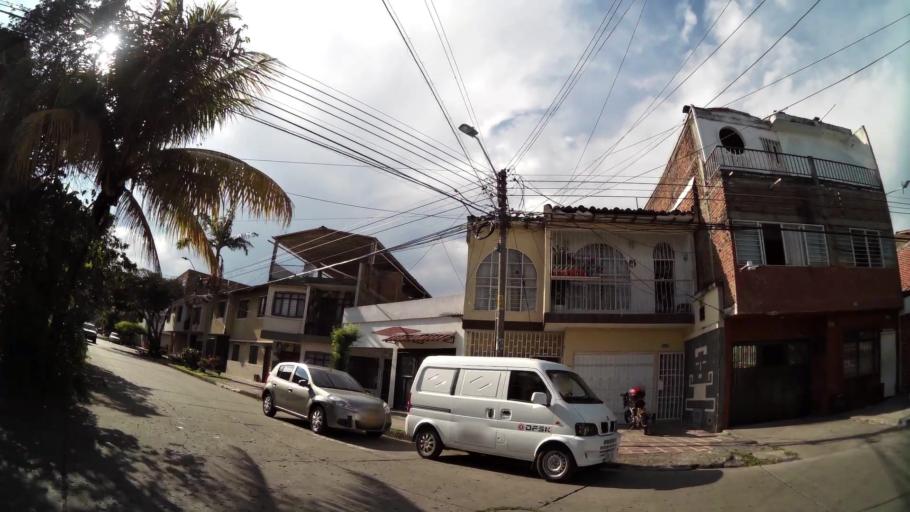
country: CO
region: Valle del Cauca
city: Cali
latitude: 3.4282
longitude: -76.5256
